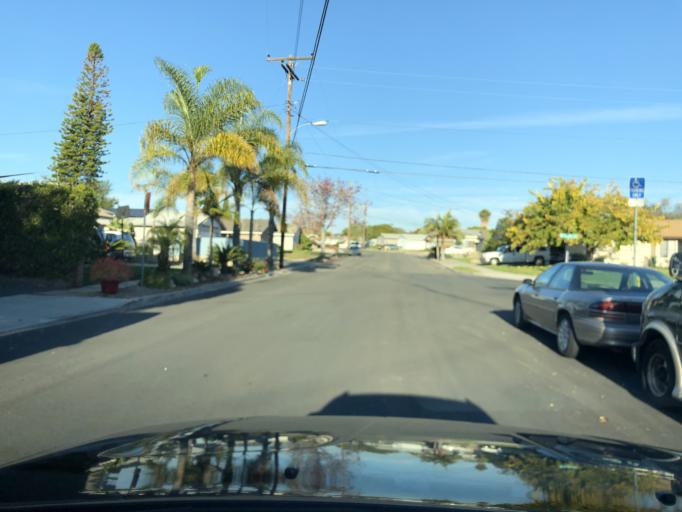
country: US
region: California
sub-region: San Diego County
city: La Jolla
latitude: 32.8191
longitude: -117.1898
